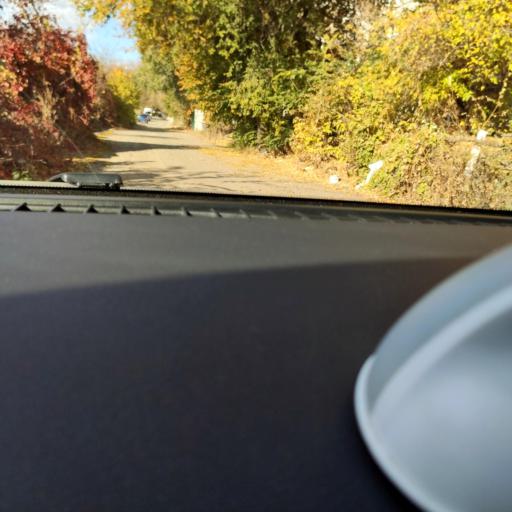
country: RU
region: Samara
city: Samara
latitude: 53.1873
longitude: 50.2151
